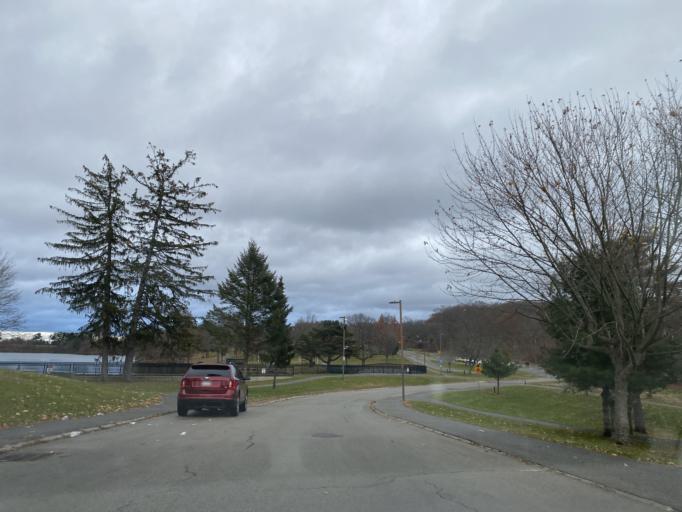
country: US
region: Massachusetts
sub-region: Worcester County
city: Worcester
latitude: 42.2815
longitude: -71.7850
